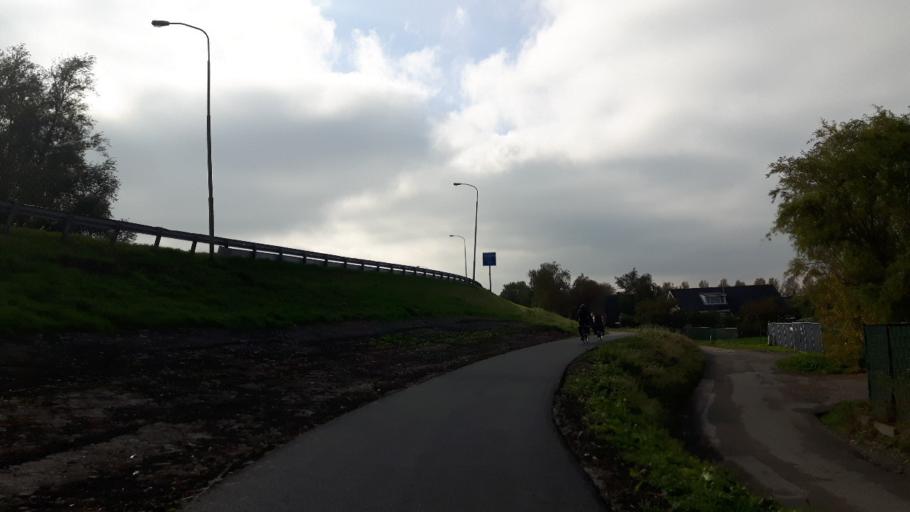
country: NL
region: South Holland
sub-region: Gemeente Gouda
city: Gouda
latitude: 51.9934
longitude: 4.6803
